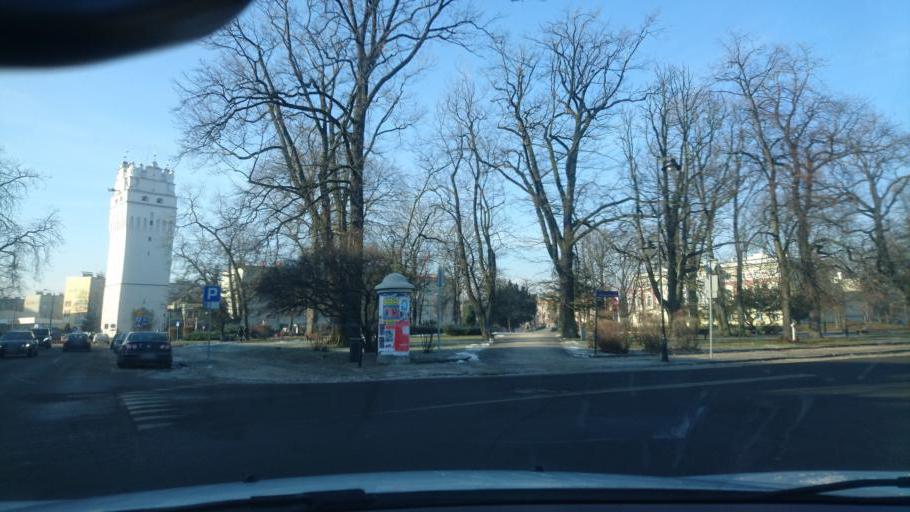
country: PL
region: Opole Voivodeship
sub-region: Powiat nyski
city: Nysa
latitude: 50.4773
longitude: 17.3363
